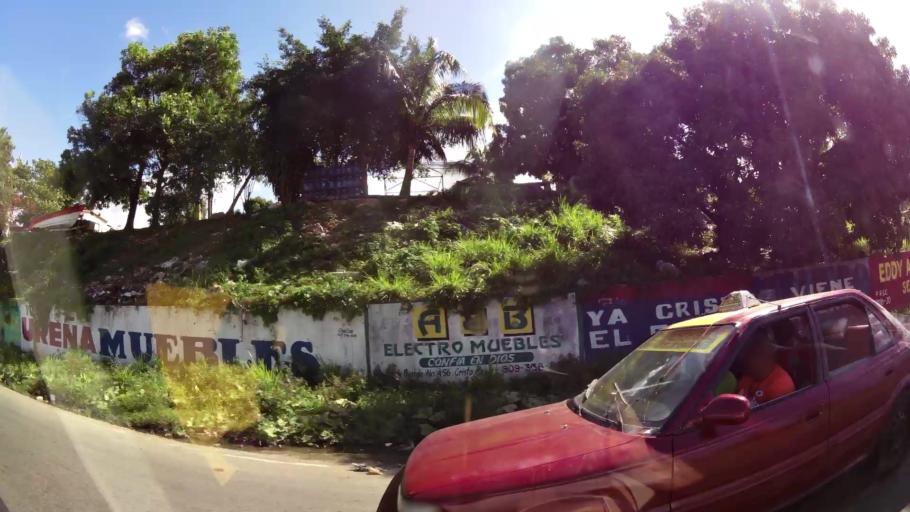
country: DO
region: Santo Domingo
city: Santo Domingo Oeste
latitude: 18.5484
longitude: -70.0438
